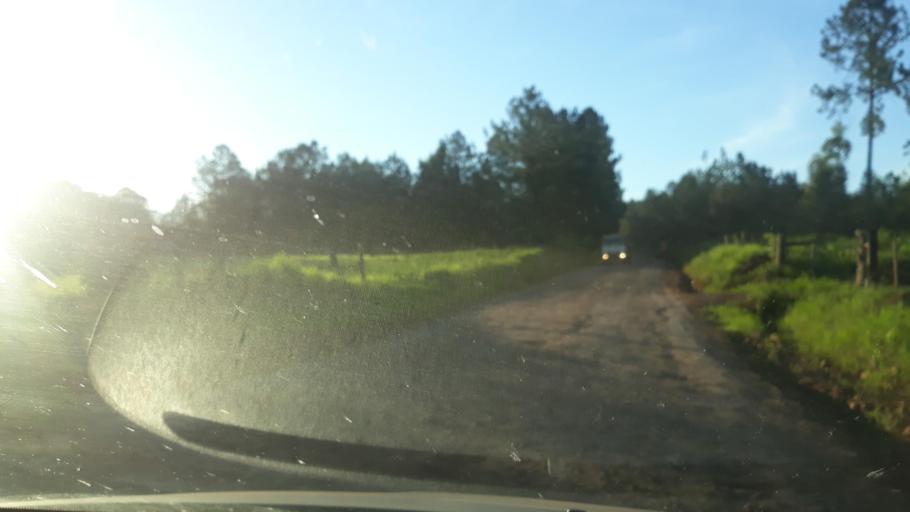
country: AR
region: Misiones
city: Ruiz de Montoya
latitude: -27.0447
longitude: -55.0045
